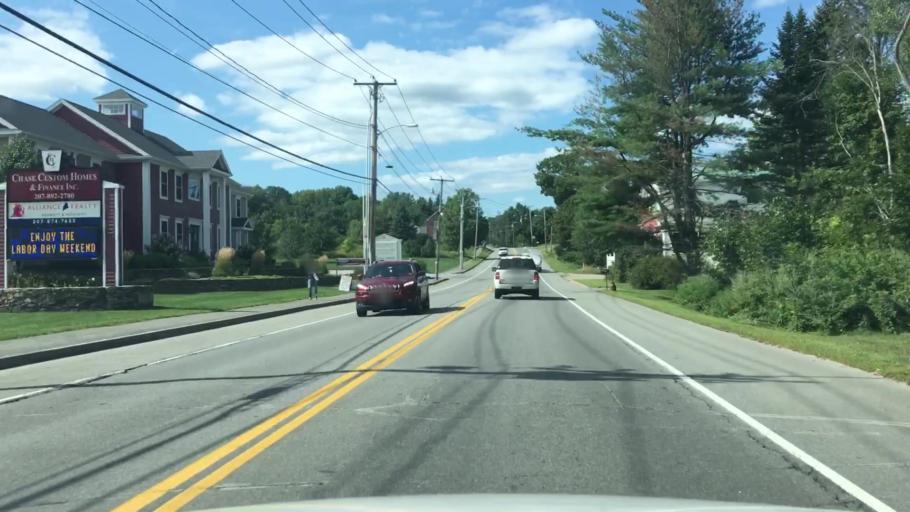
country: US
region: Maine
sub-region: Cumberland County
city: Westbrook
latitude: 43.7094
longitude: -70.3295
